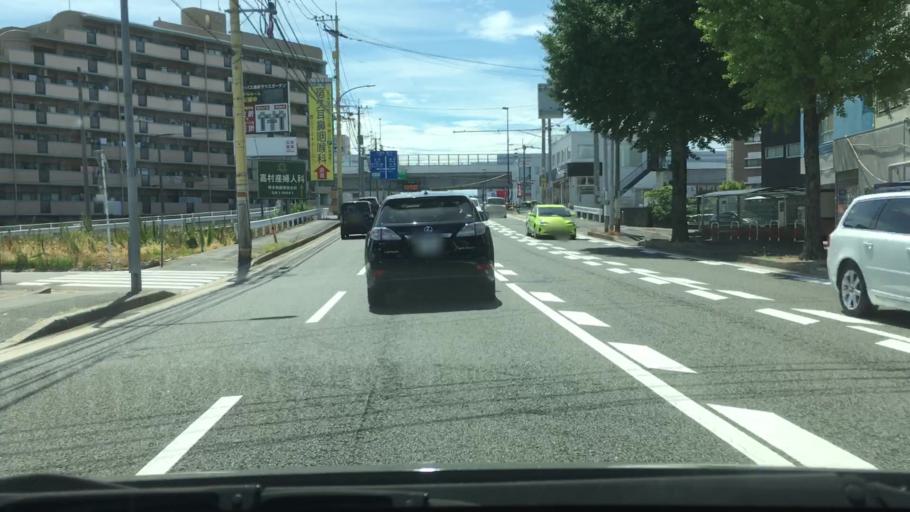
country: JP
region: Fukuoka
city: Onojo
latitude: 33.5565
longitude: 130.4524
